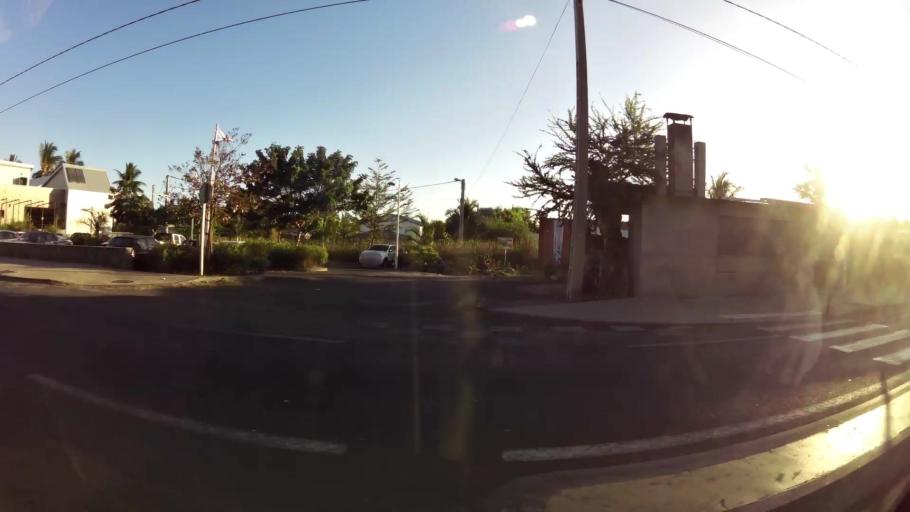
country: RE
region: Reunion
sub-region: Reunion
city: Trois-Bassins
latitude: -21.0806
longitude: 55.2297
